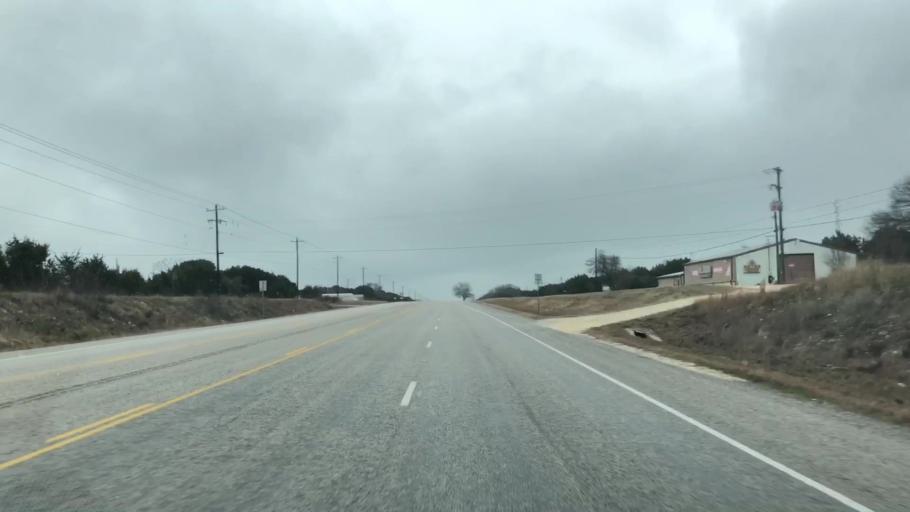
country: US
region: Texas
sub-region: Burnet County
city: Burnet
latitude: 30.8060
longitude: -98.2399
